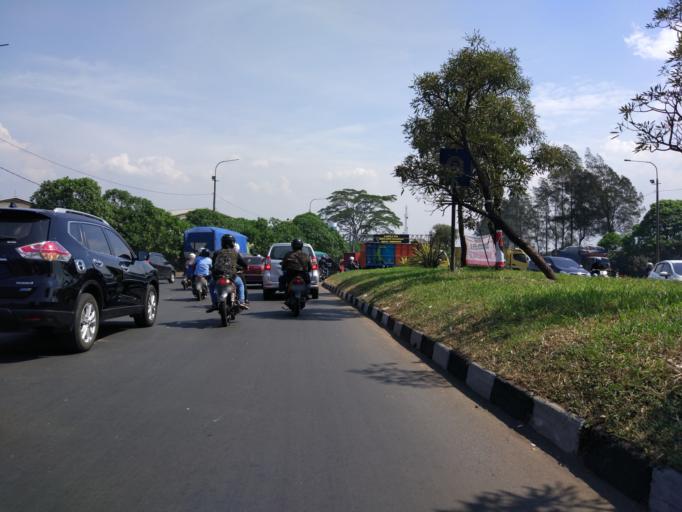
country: ID
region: West Java
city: Cileunyi
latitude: -6.9426
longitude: 107.7536
